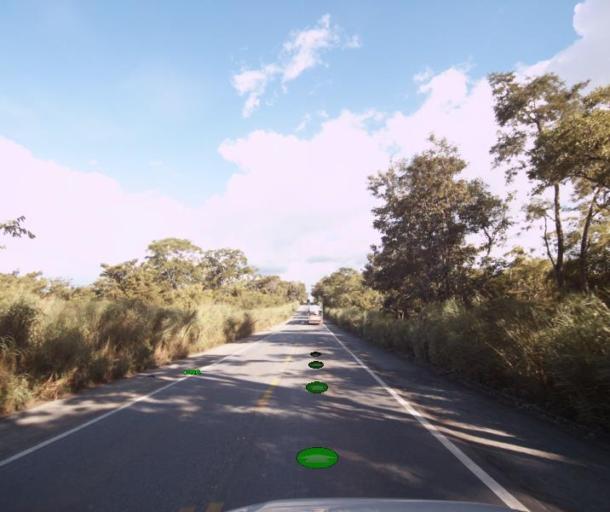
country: BR
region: Goias
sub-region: Porangatu
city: Porangatu
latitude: -13.1694
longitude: -49.1739
